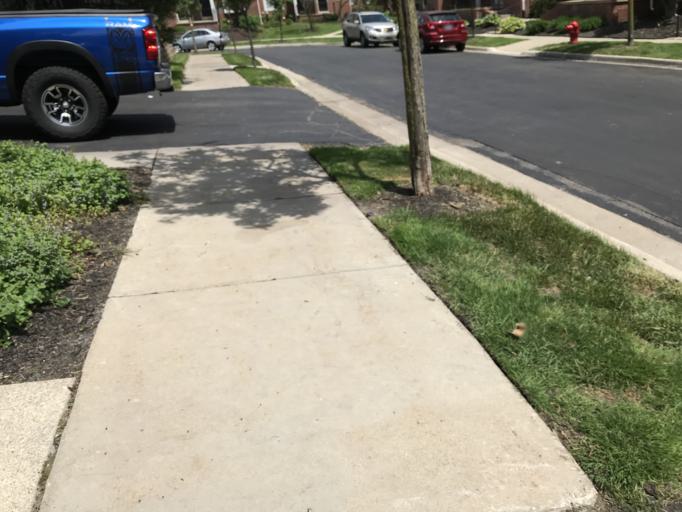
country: US
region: Michigan
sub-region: Oakland County
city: Novi
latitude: 42.4754
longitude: -83.4669
